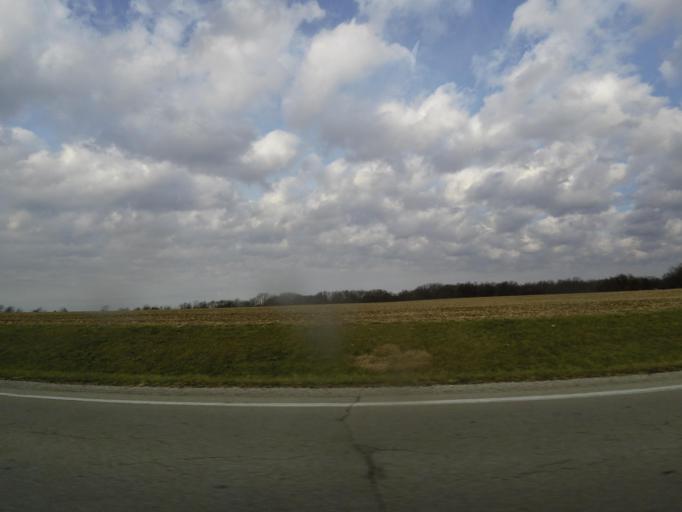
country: US
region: Illinois
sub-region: Christian County
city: Pana
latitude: 39.2986
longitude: -89.0917
